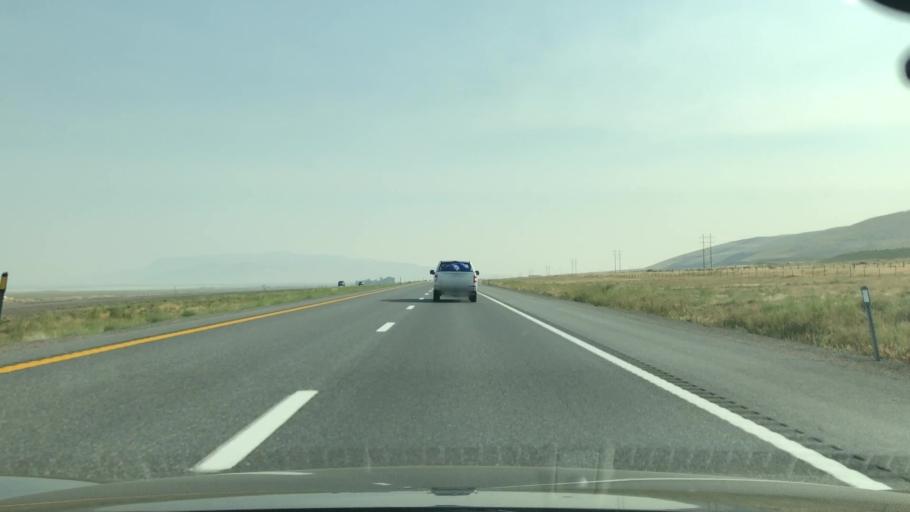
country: US
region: Nevada
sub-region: Pershing County
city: Lovelock
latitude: 40.5703
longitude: -118.2696
